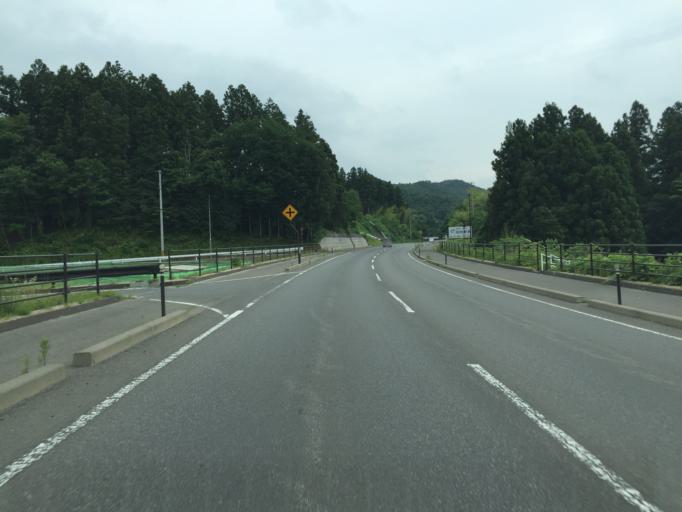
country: JP
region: Fukushima
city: Fukushima-shi
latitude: 37.7221
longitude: 140.4969
